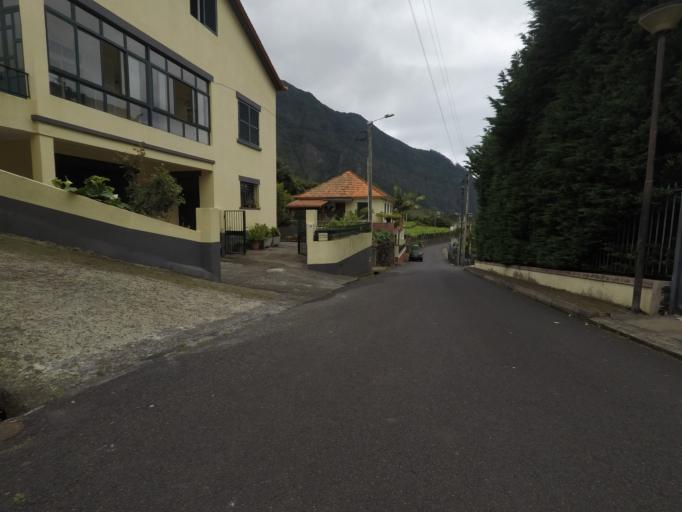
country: PT
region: Madeira
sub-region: Sao Vicente
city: Sao Vicente
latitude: 32.7910
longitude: -17.0389
